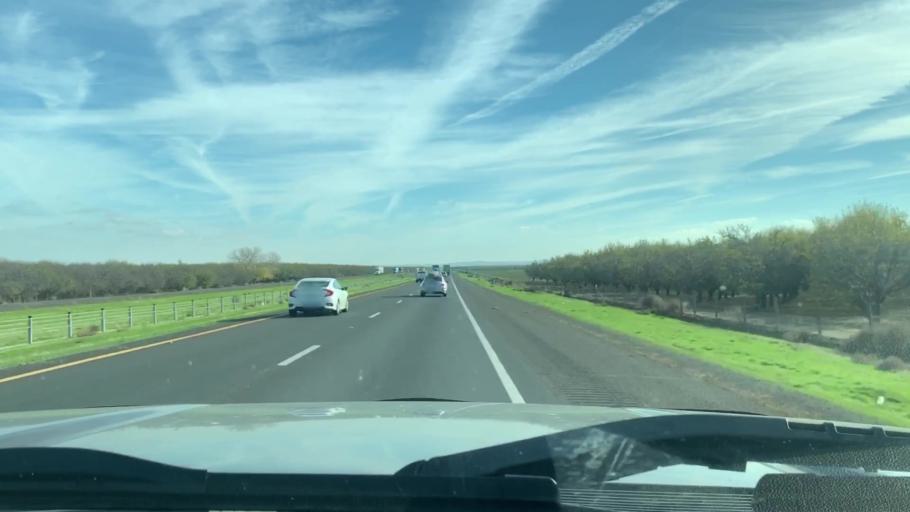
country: US
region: California
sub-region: Fresno County
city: Huron
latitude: 36.2275
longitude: -120.2273
